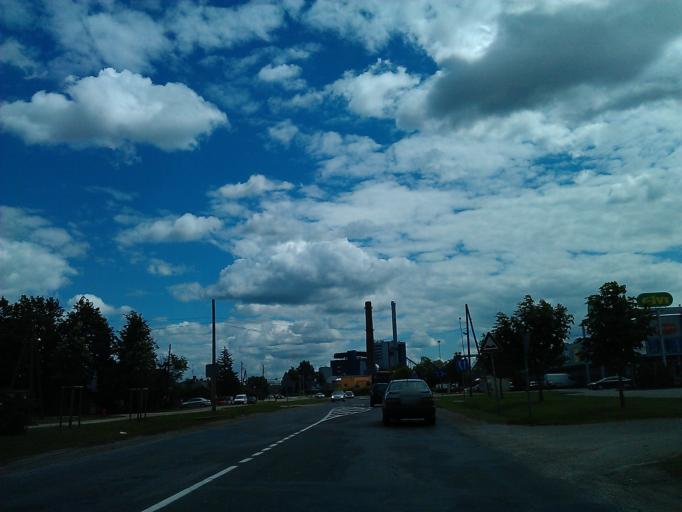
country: LV
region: Jelgava
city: Jelgava
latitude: 56.6378
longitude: 23.7038
